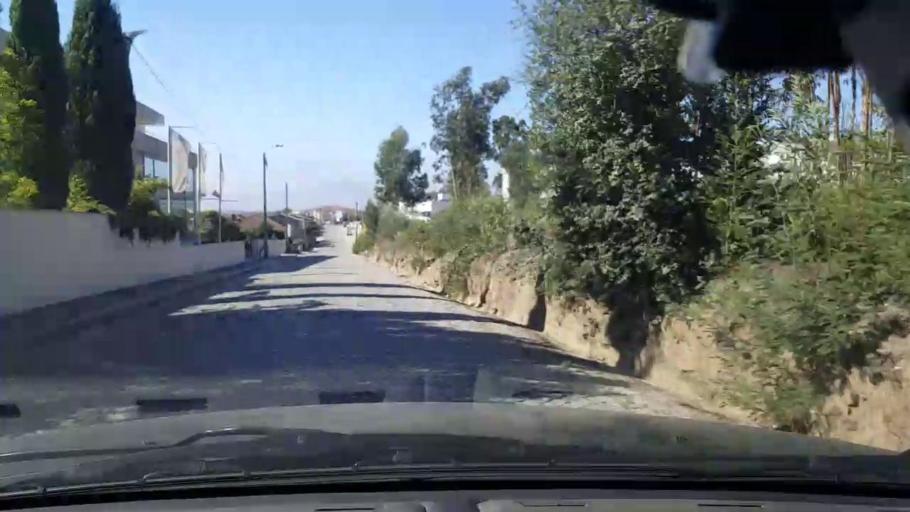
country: PT
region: Porto
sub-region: Maia
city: Anta
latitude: 41.2951
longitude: -8.6312
